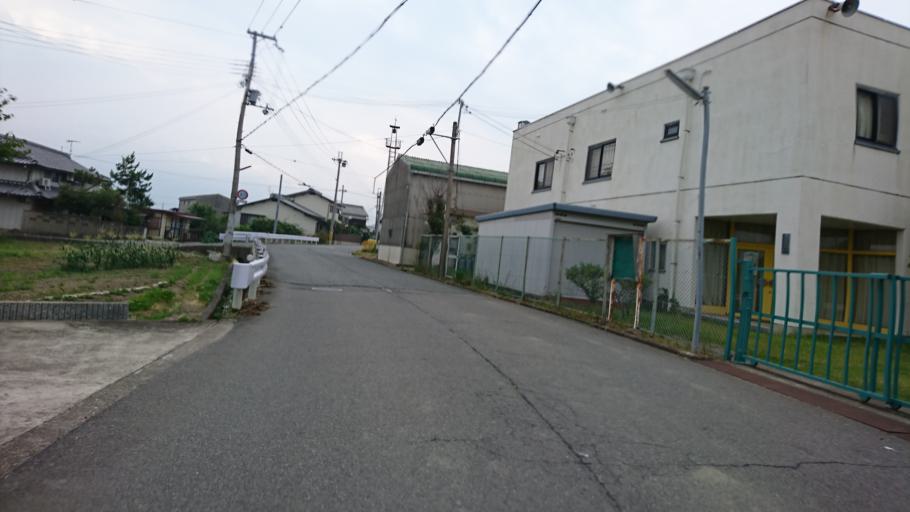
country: JP
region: Hyogo
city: Miki
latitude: 34.7398
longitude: 134.9610
